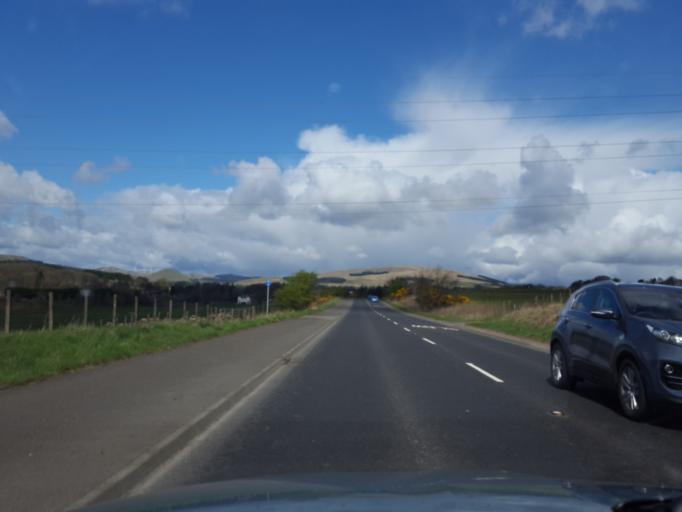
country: GB
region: Scotland
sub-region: Fife
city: Saline
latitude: 56.1703
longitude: -3.5816
